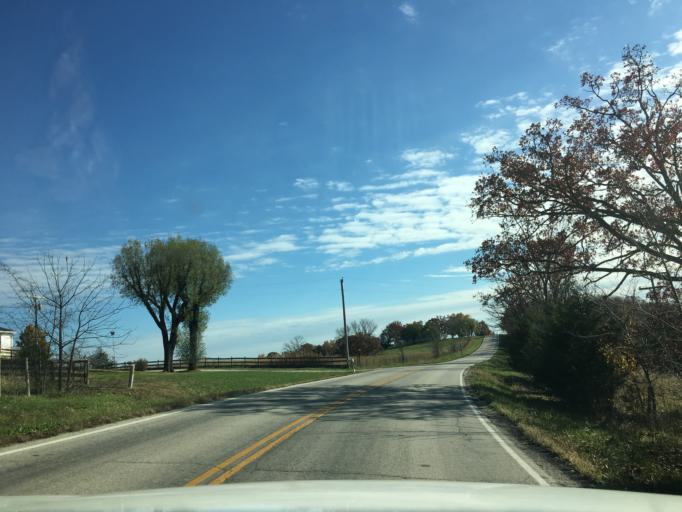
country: US
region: Missouri
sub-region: Osage County
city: Linn
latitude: 38.4372
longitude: -91.8306
